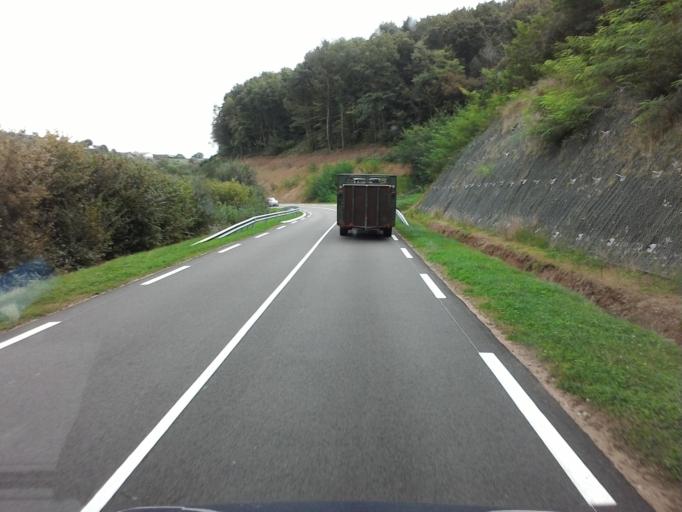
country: FR
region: Bourgogne
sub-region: Departement de Saone-et-Loire
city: Saint-Eusebe
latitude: 46.5933
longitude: 4.5030
